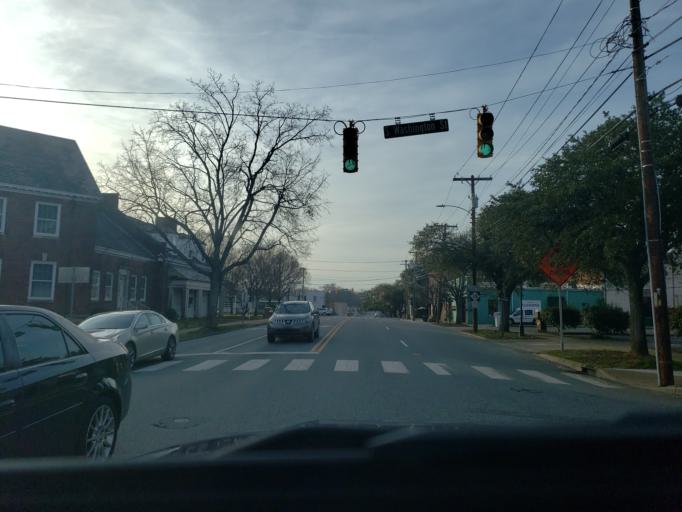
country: US
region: North Carolina
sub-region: Cleveland County
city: Shelby
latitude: 35.2894
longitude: -81.5390
